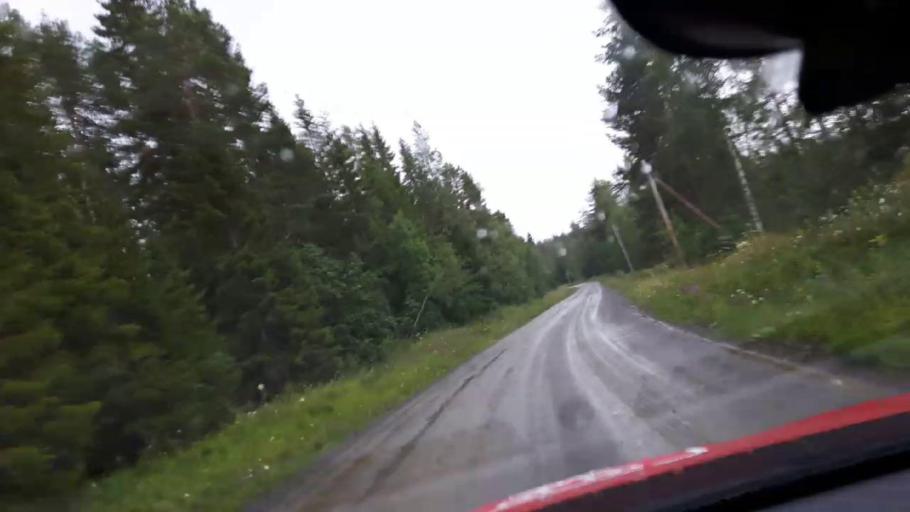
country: SE
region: Jaemtland
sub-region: OEstersunds Kommun
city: Brunflo
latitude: 62.9054
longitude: 14.8588
